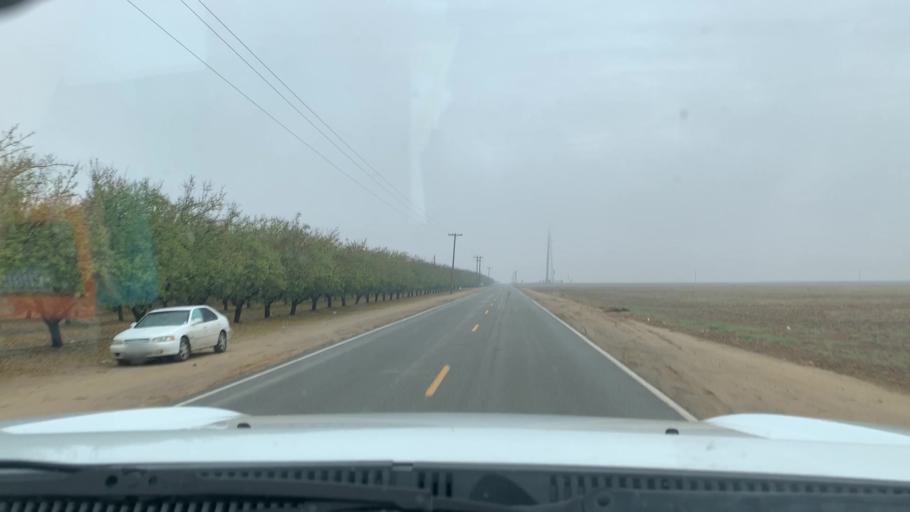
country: US
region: California
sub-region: Kern County
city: Lost Hills
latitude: 35.6172
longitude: -119.5802
